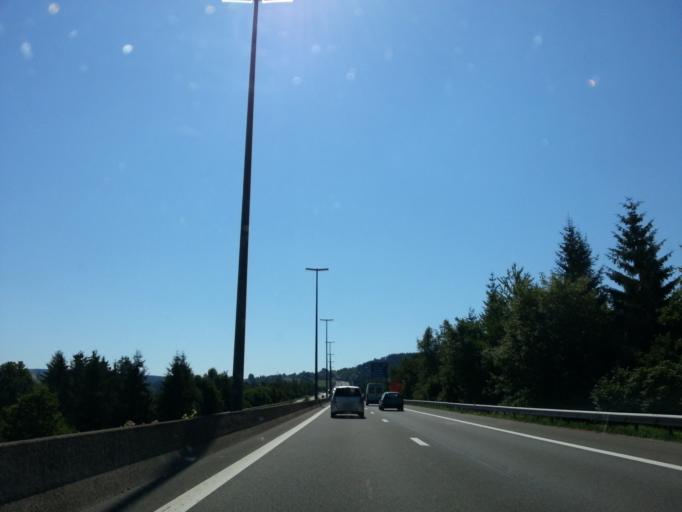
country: BE
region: Wallonia
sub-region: Province de Liege
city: Malmedy
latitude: 50.3726
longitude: 6.0168
